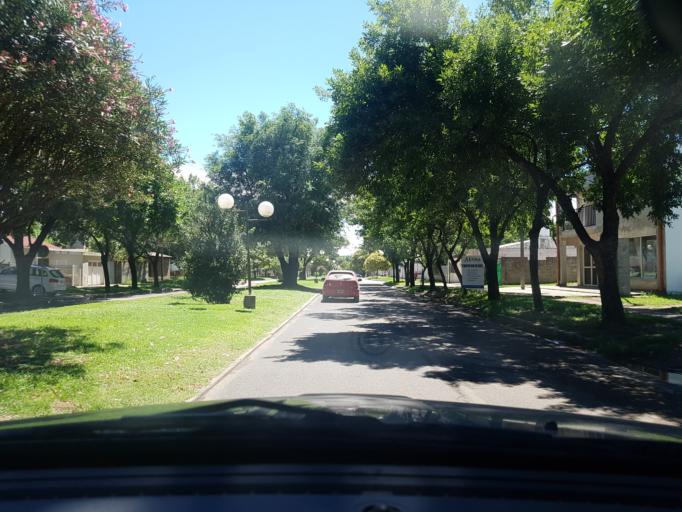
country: AR
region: Cordoba
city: Las Perdices
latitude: -32.7574
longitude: -63.7833
